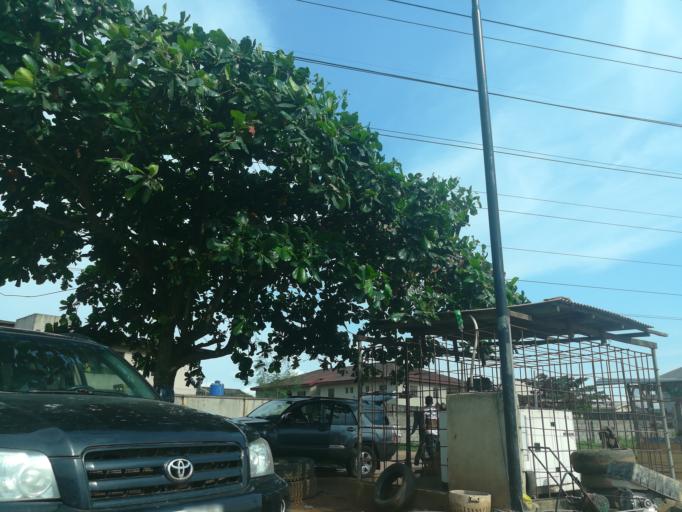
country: NG
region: Lagos
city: Ikorodu
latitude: 6.6323
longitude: 3.5116
